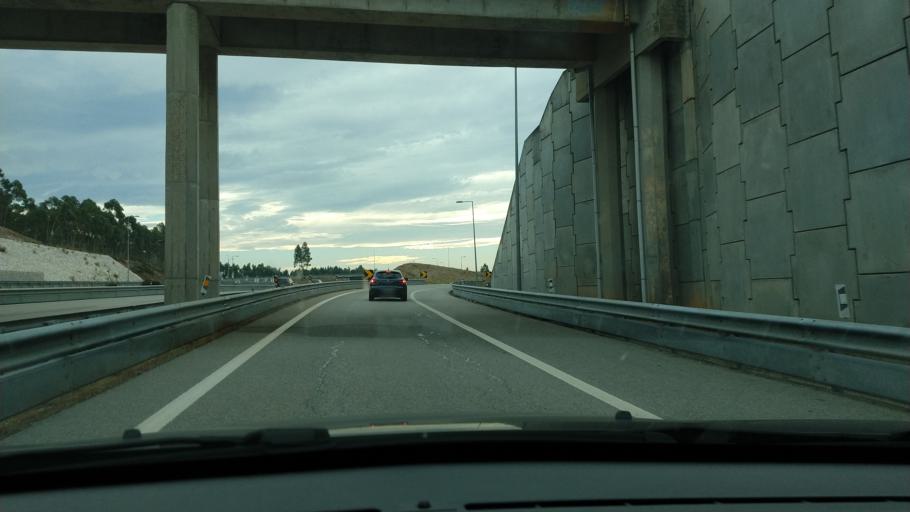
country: PT
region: Coimbra
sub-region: Figueira da Foz
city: Alhadas
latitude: 40.1535
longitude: -8.7858
